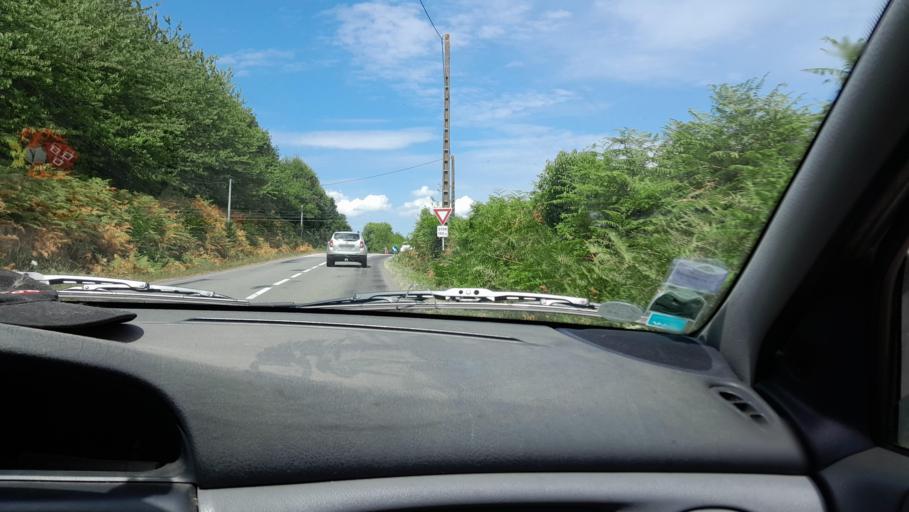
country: FR
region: Brittany
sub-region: Departement d'Ille-et-Vilaine
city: Luitre
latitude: 48.2760
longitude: -1.1503
